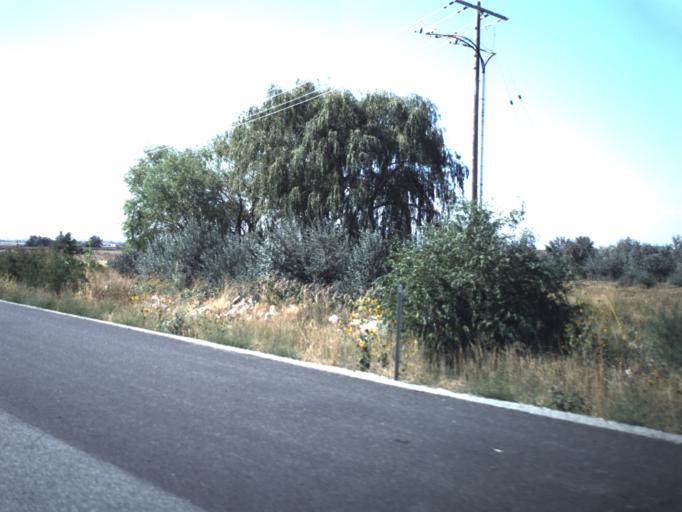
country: US
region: Utah
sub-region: Box Elder County
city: Perry
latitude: 41.4866
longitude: -112.0356
